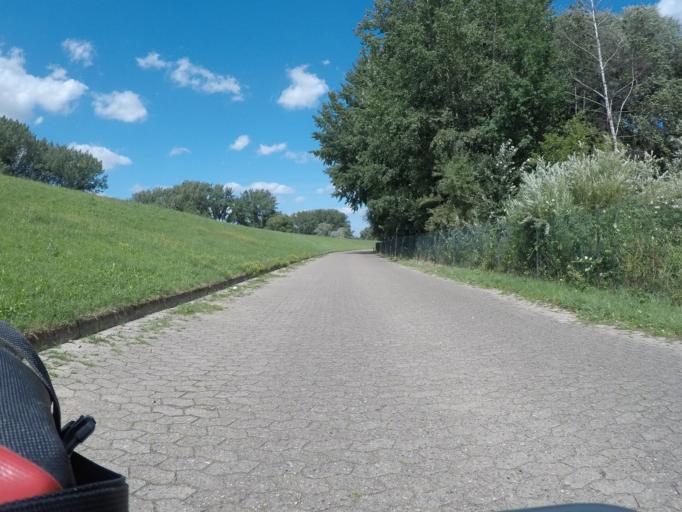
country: DE
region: Hamburg
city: Rothenburgsort
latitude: 53.5041
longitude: 10.0640
